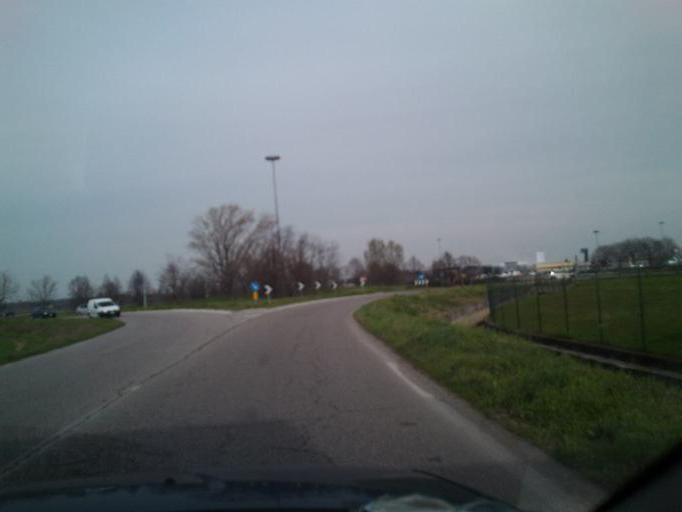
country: IT
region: Lombardy
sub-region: Provincia di Mantova
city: Sant'Antonio
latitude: 45.1901
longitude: 10.7685
